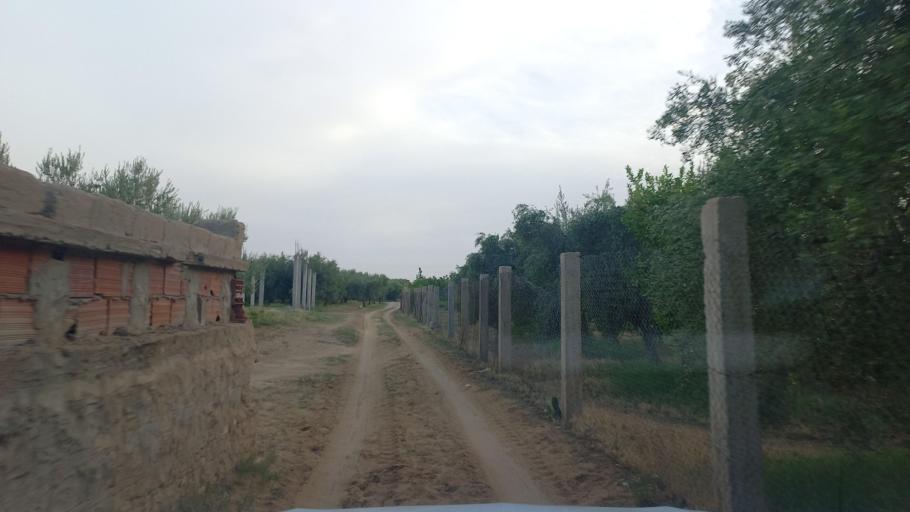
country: TN
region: Al Qasrayn
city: Kasserine
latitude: 35.2177
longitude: 9.0525
